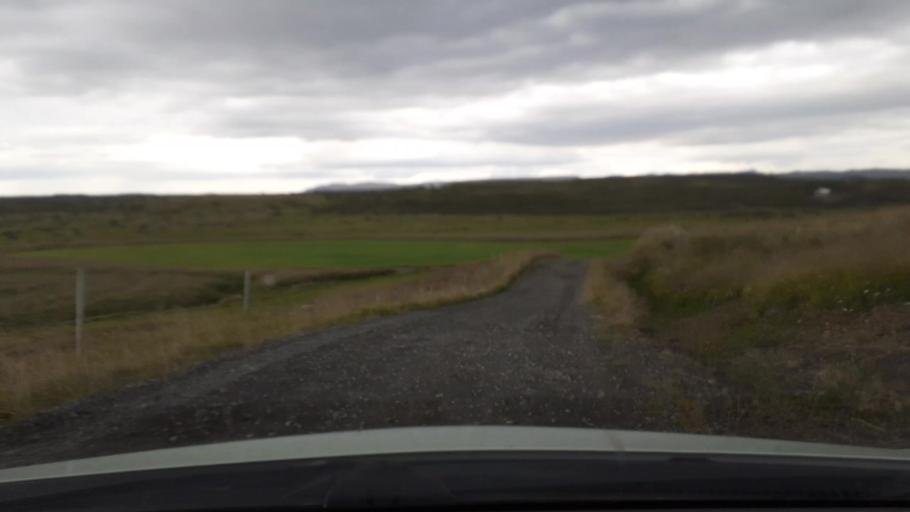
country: IS
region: West
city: Borgarnes
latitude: 64.6379
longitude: -21.7387
